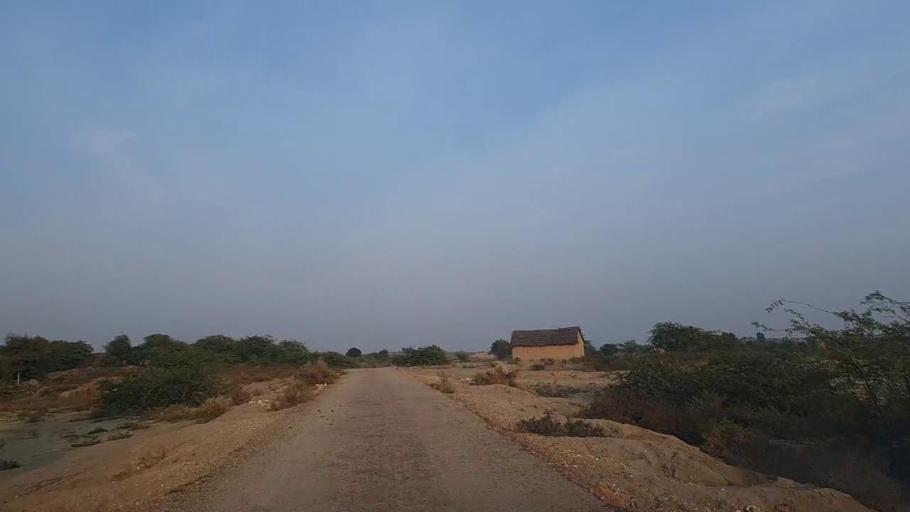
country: PK
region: Sindh
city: Jam Sahib
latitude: 26.4106
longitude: 68.6031
